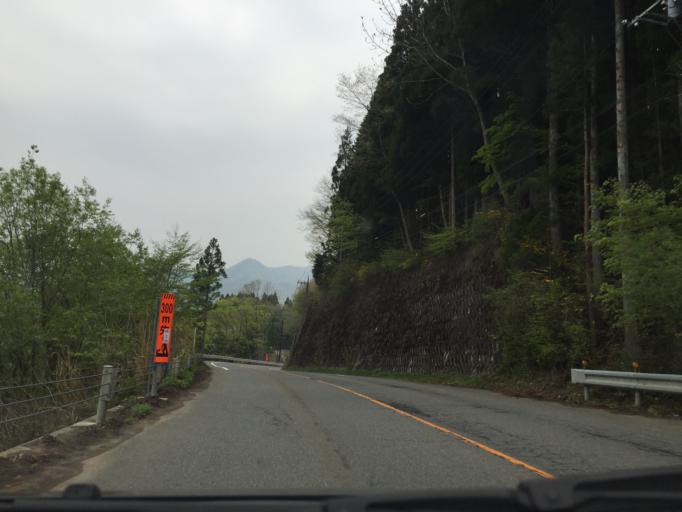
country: JP
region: Tochigi
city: Nikko
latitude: 36.9369
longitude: 139.6953
